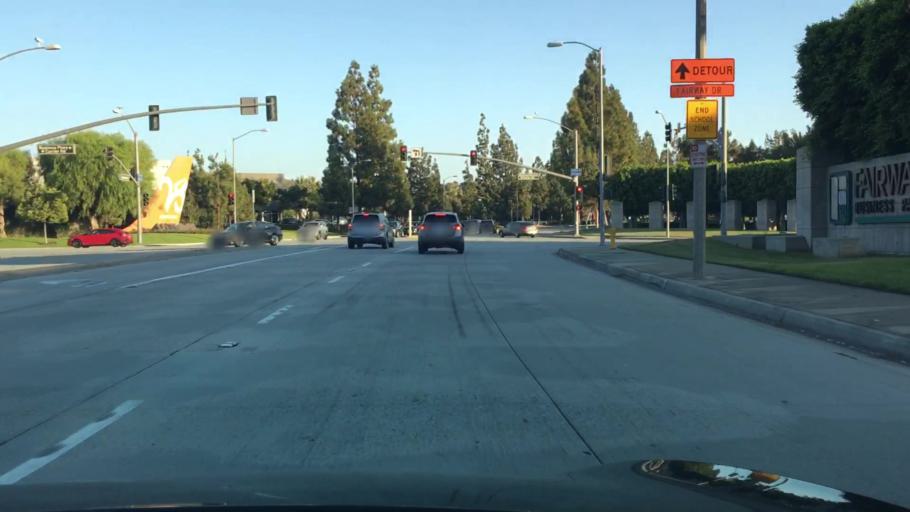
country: US
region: California
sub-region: Los Angeles County
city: Walnut
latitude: 34.0064
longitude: -117.8559
